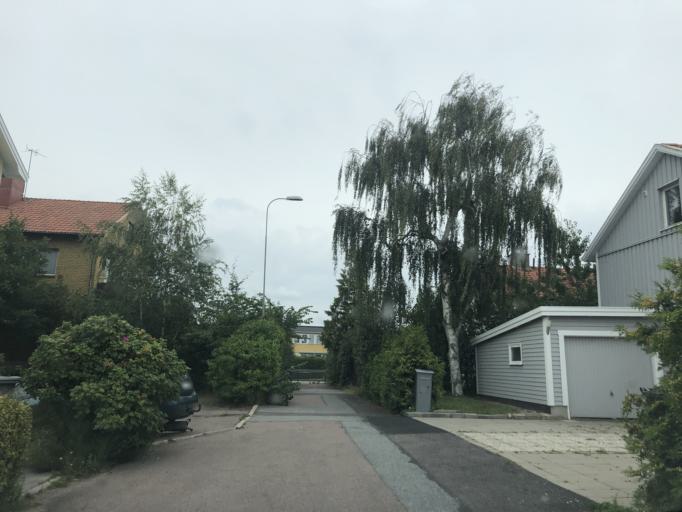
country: SE
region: Vaestra Goetaland
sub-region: Goteborg
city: Goeteborg
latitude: 57.7251
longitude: 11.9340
